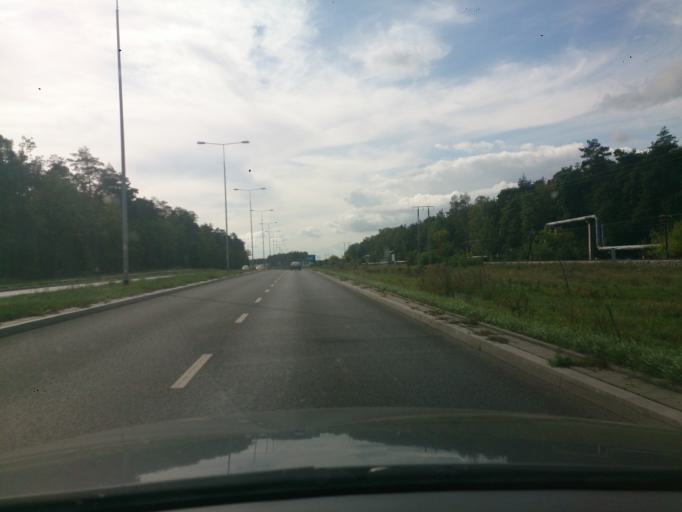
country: PL
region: Kujawsko-Pomorskie
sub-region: Grudziadz
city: Grudziadz
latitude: 53.4569
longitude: 18.7400
